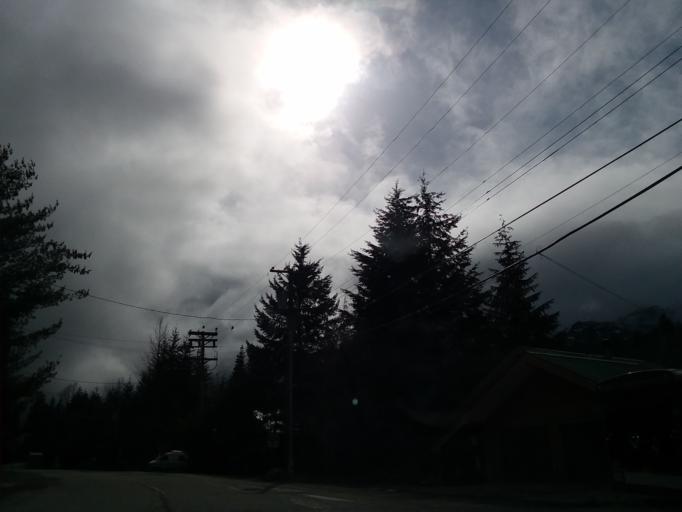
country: CA
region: British Columbia
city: Whistler
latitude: 50.1263
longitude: -122.9568
